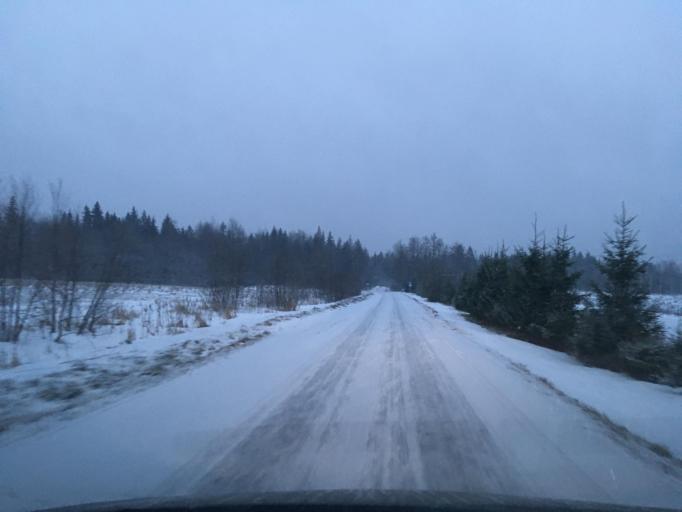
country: EE
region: Harju
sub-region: Nissi vald
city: Riisipere
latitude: 59.1769
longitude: 24.3679
